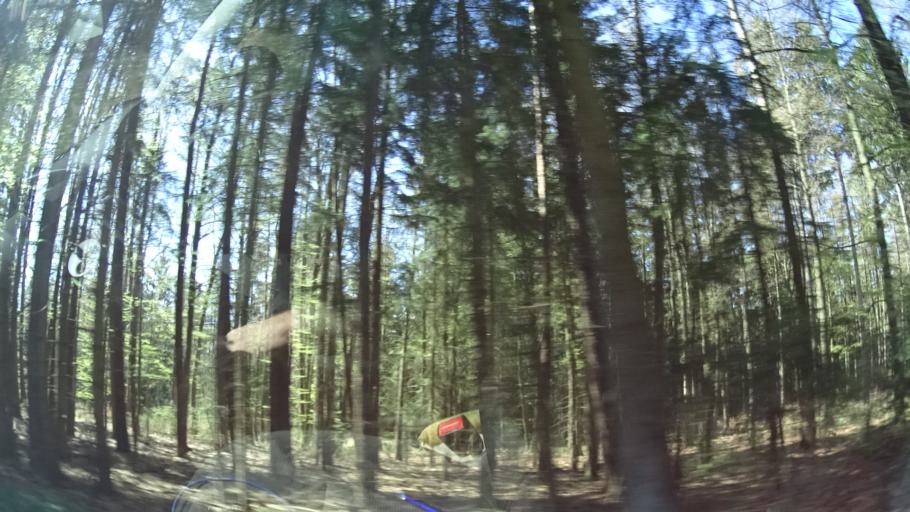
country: DE
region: Bavaria
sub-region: Upper Palatinate
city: Lauterhofen
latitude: 49.4117
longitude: 11.6014
